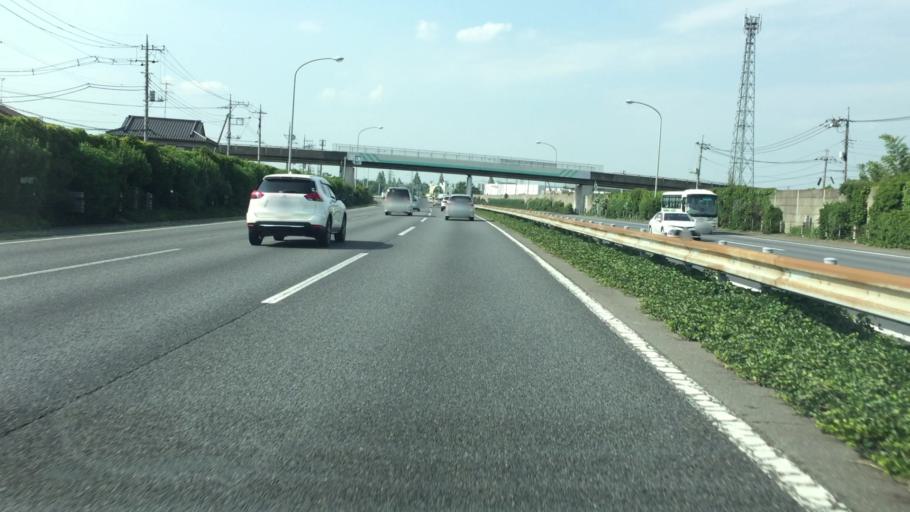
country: JP
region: Saitama
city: Shiraoka
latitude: 36.0135
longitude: 139.6748
